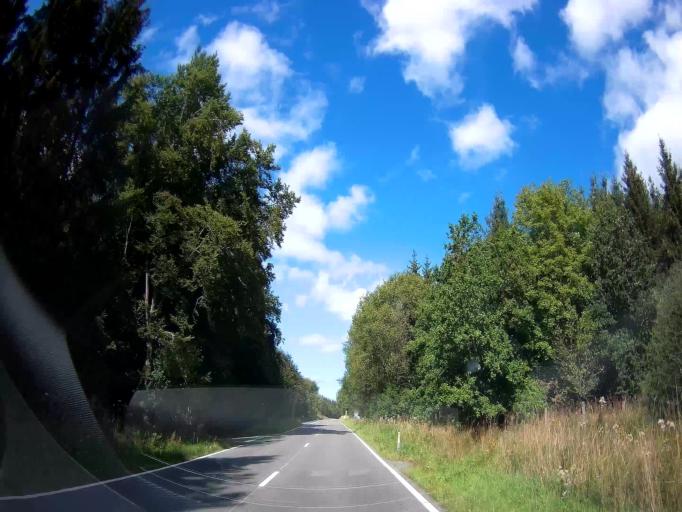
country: BE
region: Wallonia
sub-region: Province du Luxembourg
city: Bastogne
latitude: 50.0354
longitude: 5.6961
